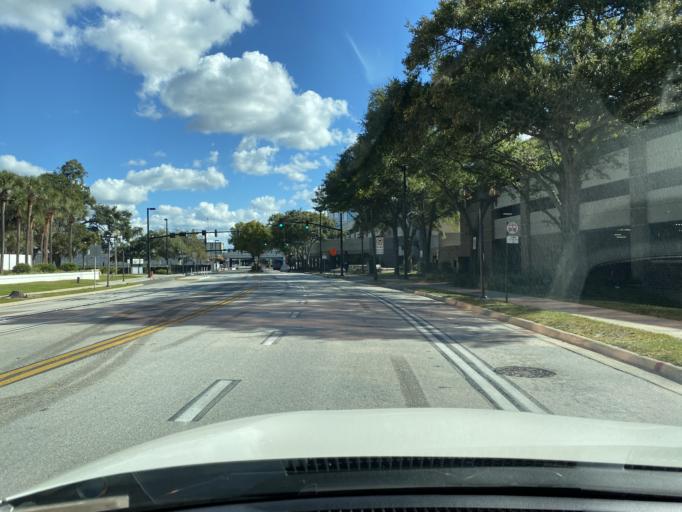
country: US
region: Florida
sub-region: Orange County
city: Orlando
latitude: 28.5495
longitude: -81.3850
